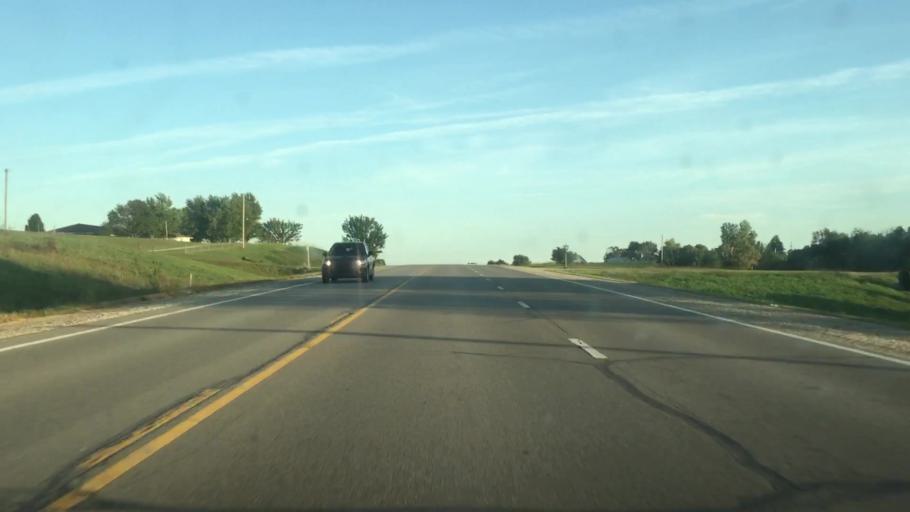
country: US
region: Kansas
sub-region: Atchison County
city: Atchison
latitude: 39.4784
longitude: -95.1058
